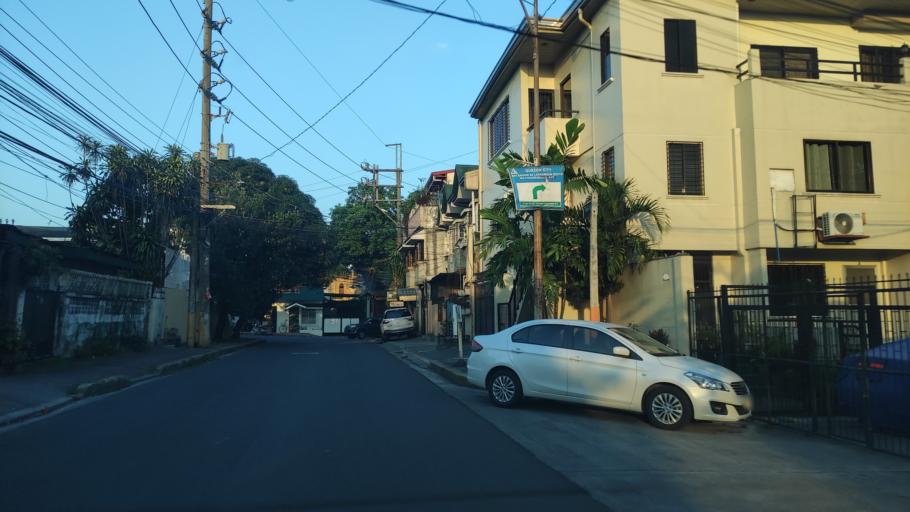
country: PH
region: Calabarzon
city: Bagong Pagasa
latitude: 14.6728
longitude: 121.0225
